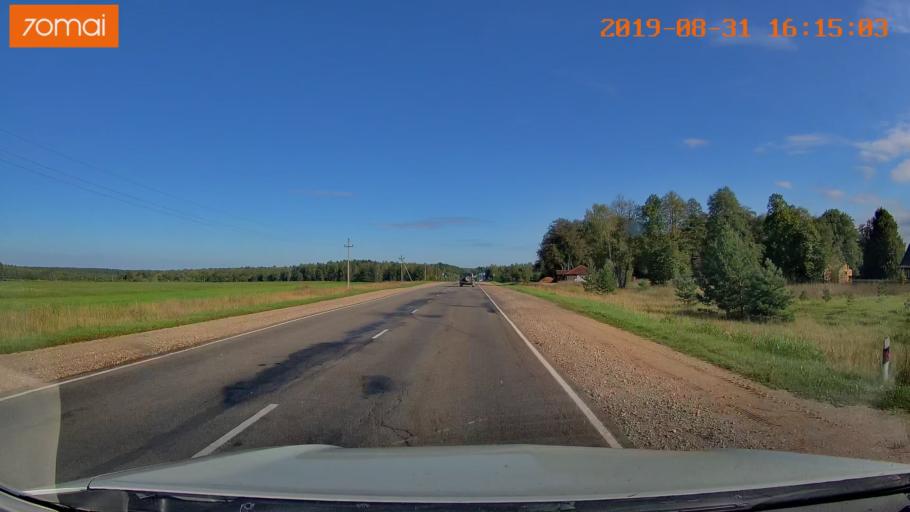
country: RU
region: Kaluga
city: Nikola-Lenivets
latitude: 54.5624
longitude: 35.4803
